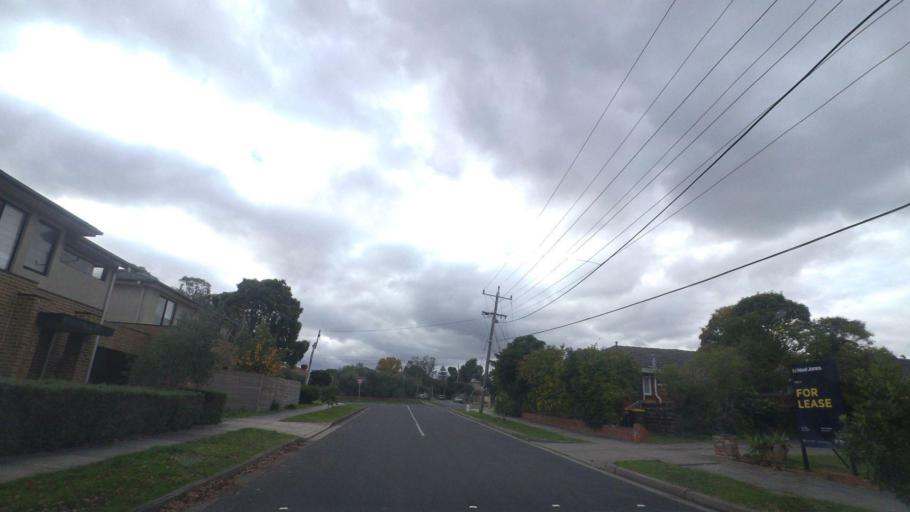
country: AU
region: Victoria
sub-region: Whitehorse
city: Nunawading
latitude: -37.8159
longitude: 145.1702
